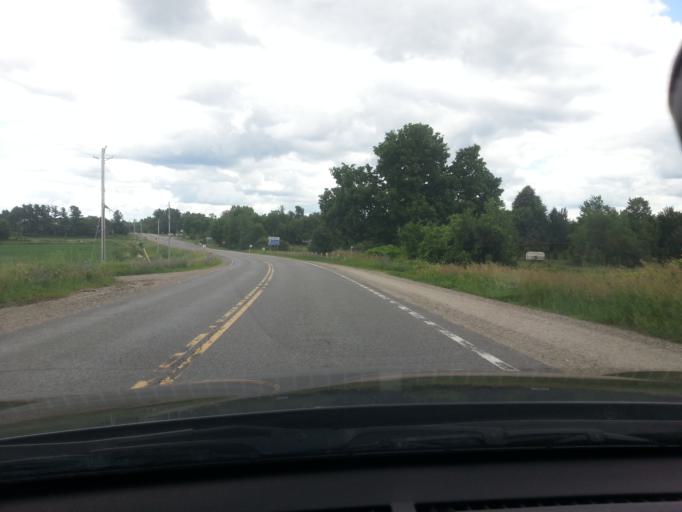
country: CA
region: Ontario
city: Perth
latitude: 44.6355
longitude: -76.2539
